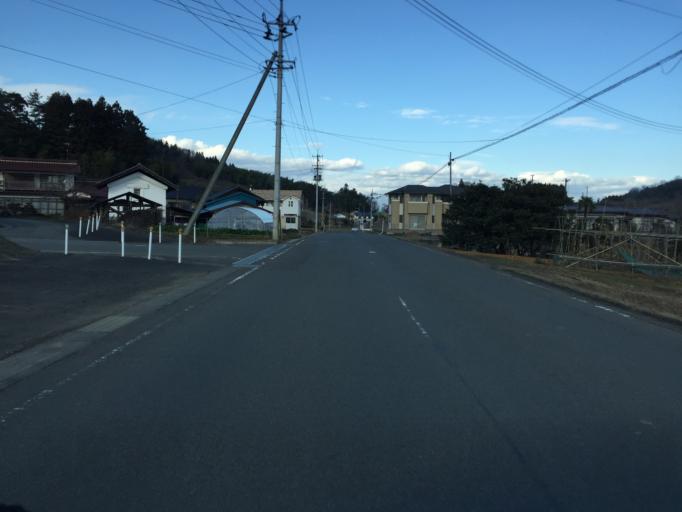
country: JP
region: Fukushima
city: Fukushima-shi
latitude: 37.7188
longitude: 140.4254
